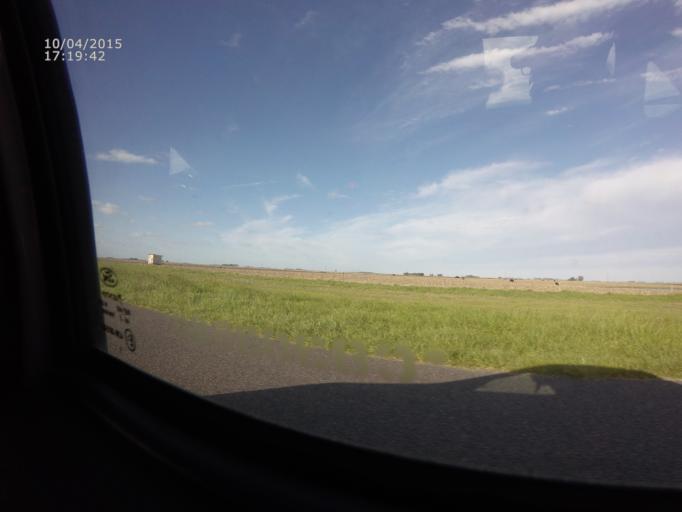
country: AR
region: Buenos Aires
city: Coronel Vidal
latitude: -37.1601
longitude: -57.8106
